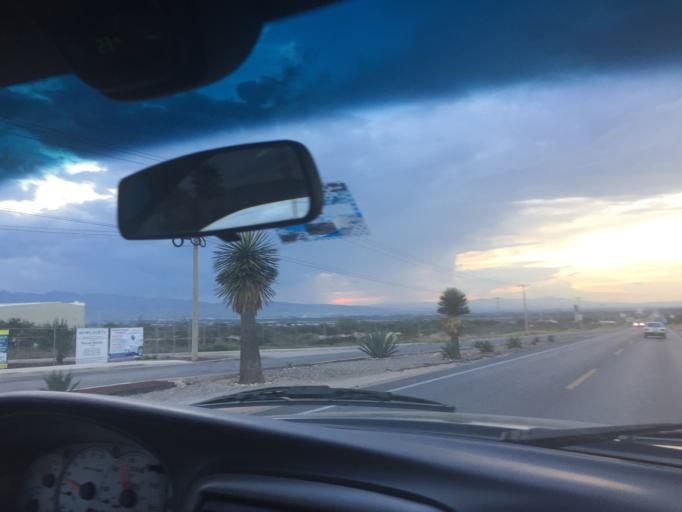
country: MX
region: San Luis Potosi
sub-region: San Luis Potosi
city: Ciudad Satelite
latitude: 22.1255
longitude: -100.8177
